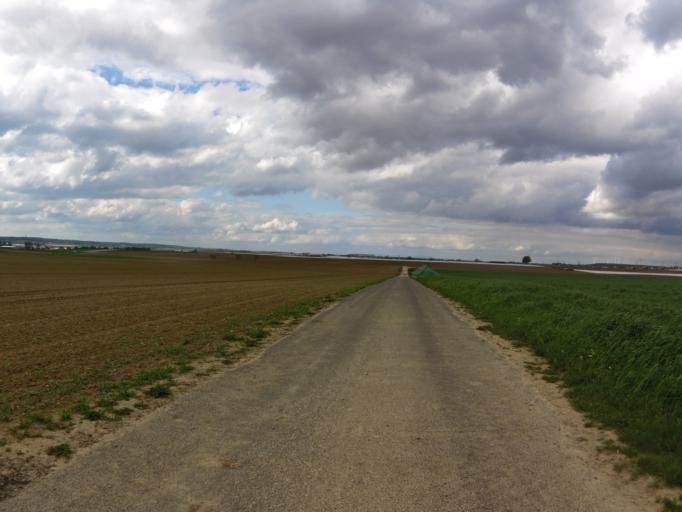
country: DE
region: Bavaria
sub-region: Regierungsbezirk Unterfranken
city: Oberpleichfeld
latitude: 49.8599
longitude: 10.0790
